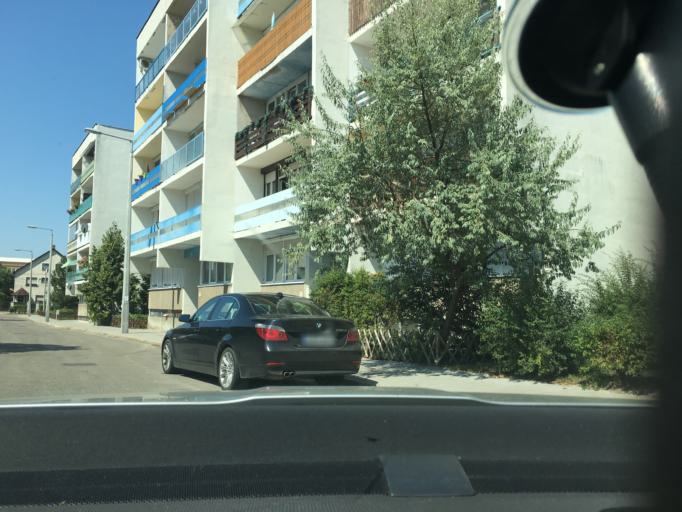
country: HU
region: Budapest
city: Budapest XVI. keruelet
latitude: 47.5076
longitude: 19.1908
